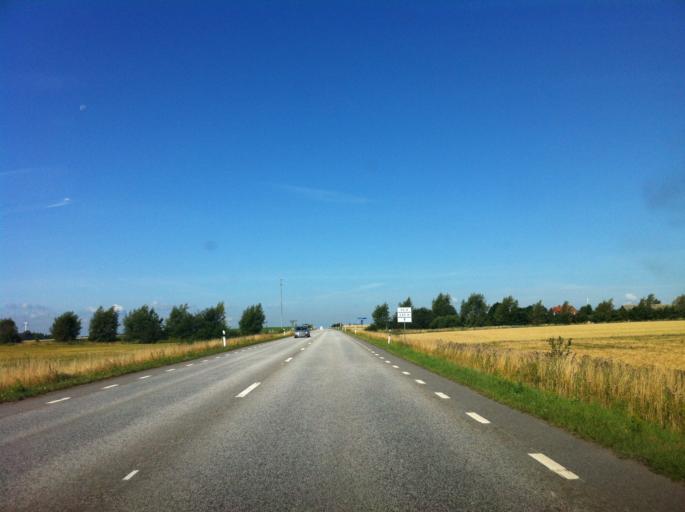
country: SE
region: Skane
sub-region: Landskrona
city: Asmundtorp
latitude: 55.8905
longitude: 12.9446
